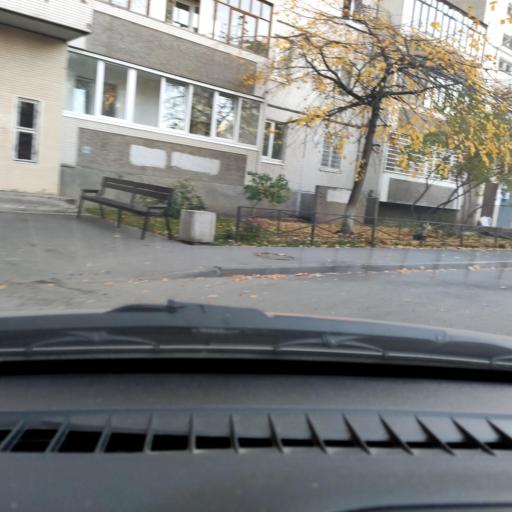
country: RU
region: Samara
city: Tol'yatti
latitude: 53.5386
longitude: 49.3506
